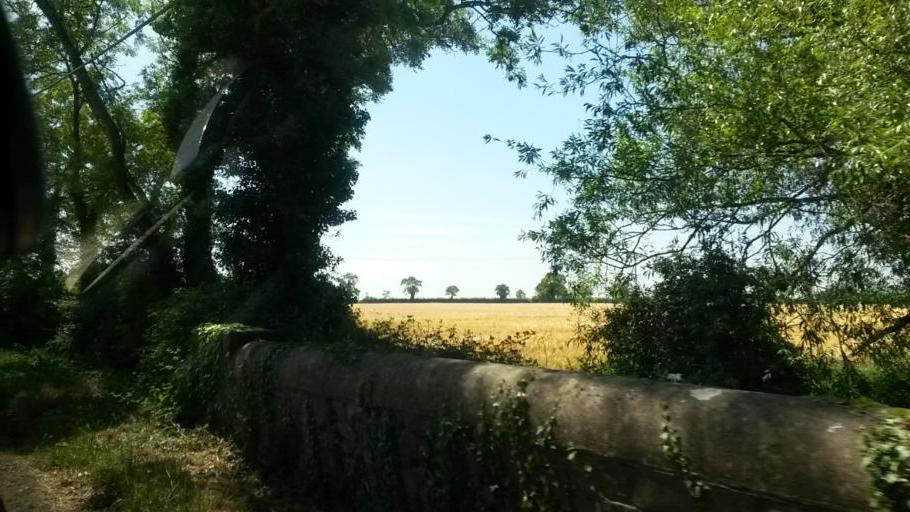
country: IE
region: Leinster
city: Balrothery
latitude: 53.5355
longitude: -6.2373
